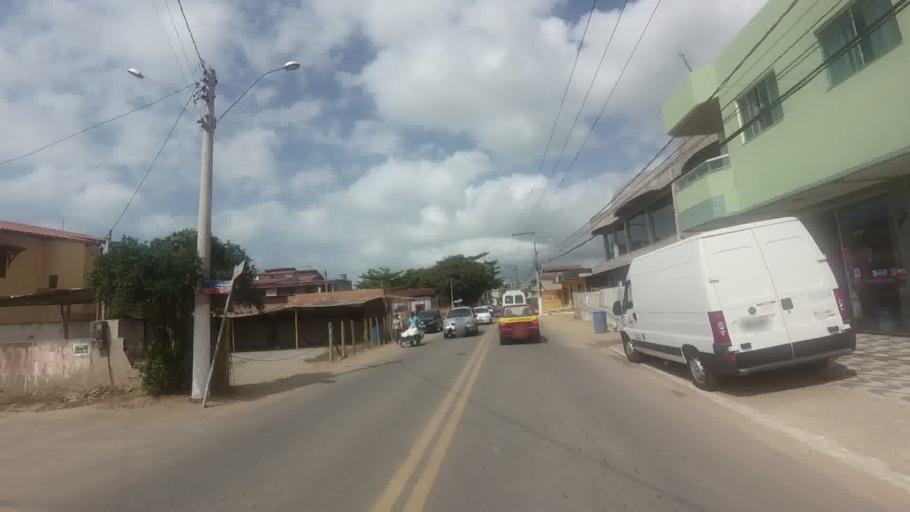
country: BR
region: Espirito Santo
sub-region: Piuma
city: Piuma
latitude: -20.9024
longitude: -40.7789
